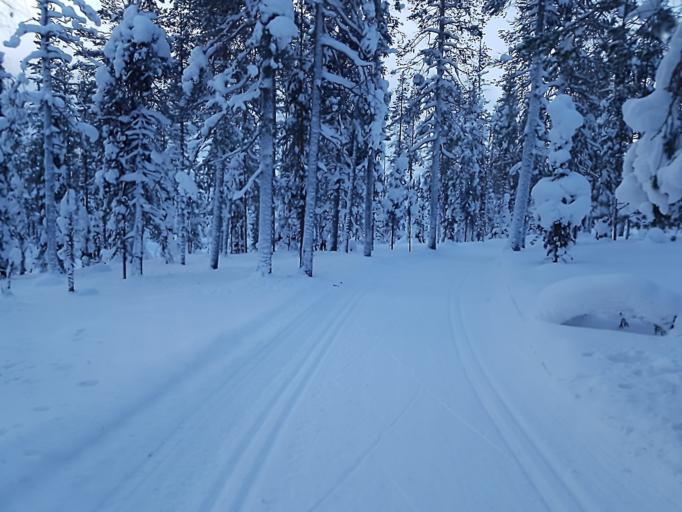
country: FI
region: Lapland
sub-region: Tunturi-Lappi
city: Kolari
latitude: 67.6419
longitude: 24.2339
